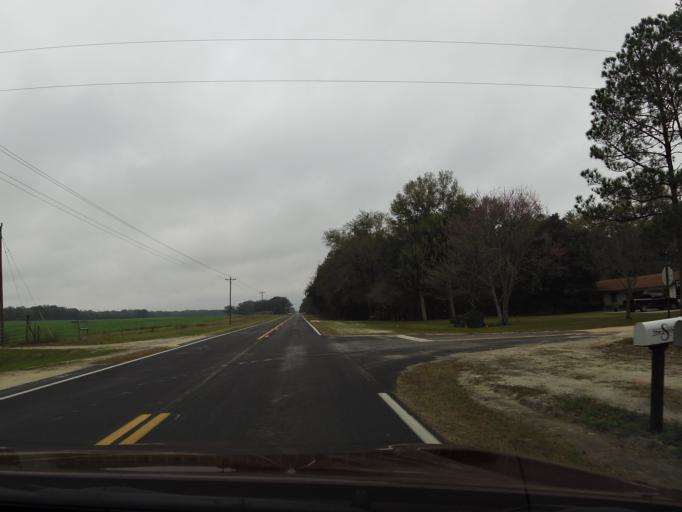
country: US
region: Florida
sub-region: Gilchrist County
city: Trenton
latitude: 29.7961
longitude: -82.8707
